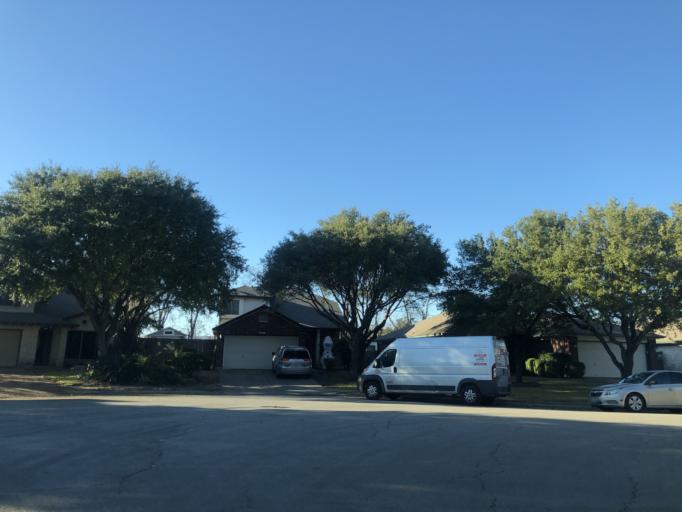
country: US
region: Texas
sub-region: Travis County
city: Windemere
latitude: 30.4791
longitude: -97.6585
